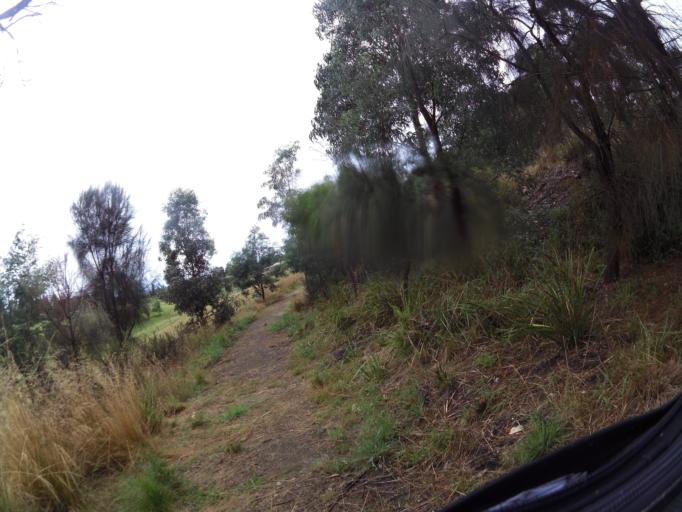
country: AU
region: Victoria
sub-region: East Gippsland
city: Bairnsdale
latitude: -37.8116
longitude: 147.7440
